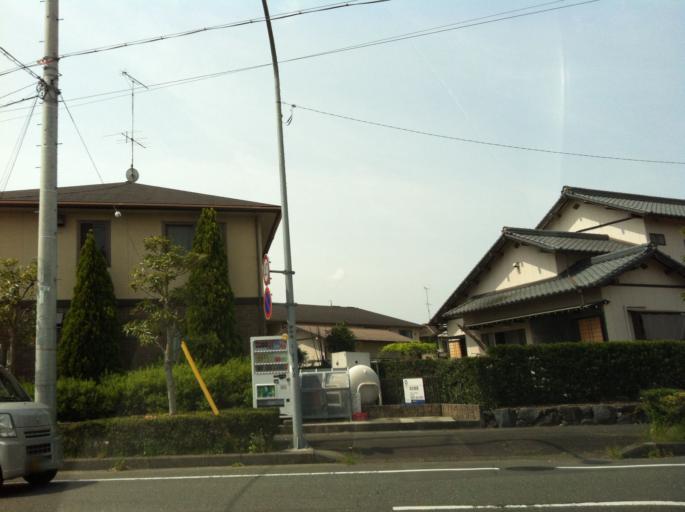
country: JP
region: Shizuoka
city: Kakegawa
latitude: 34.7747
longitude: 138.0030
